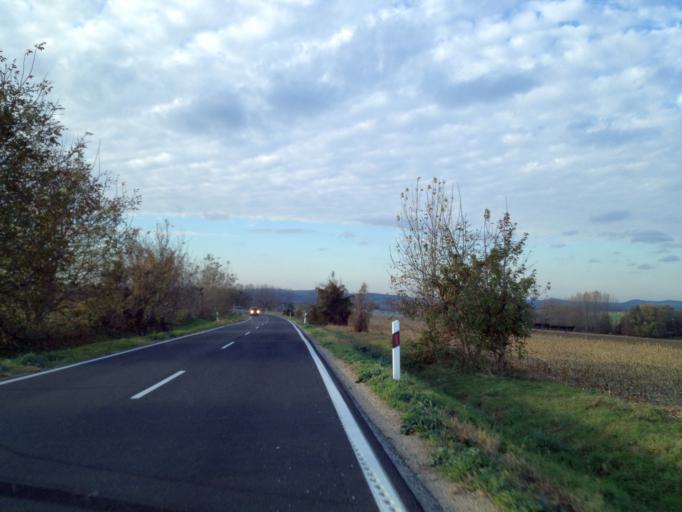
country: HU
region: Gyor-Moson-Sopron
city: Bakonyszentlaszlo
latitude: 47.4269
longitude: 17.8383
